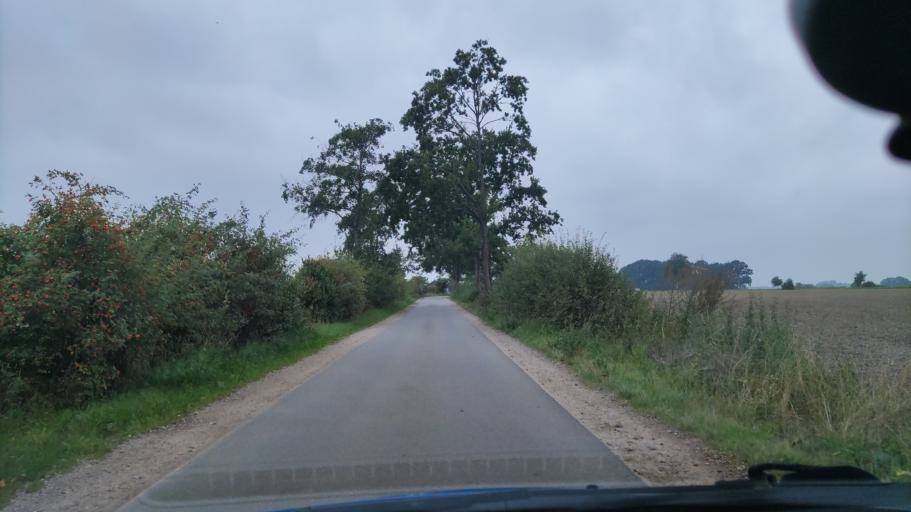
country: DE
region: Lower Saxony
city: Romstedt
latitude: 53.1184
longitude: 10.6322
